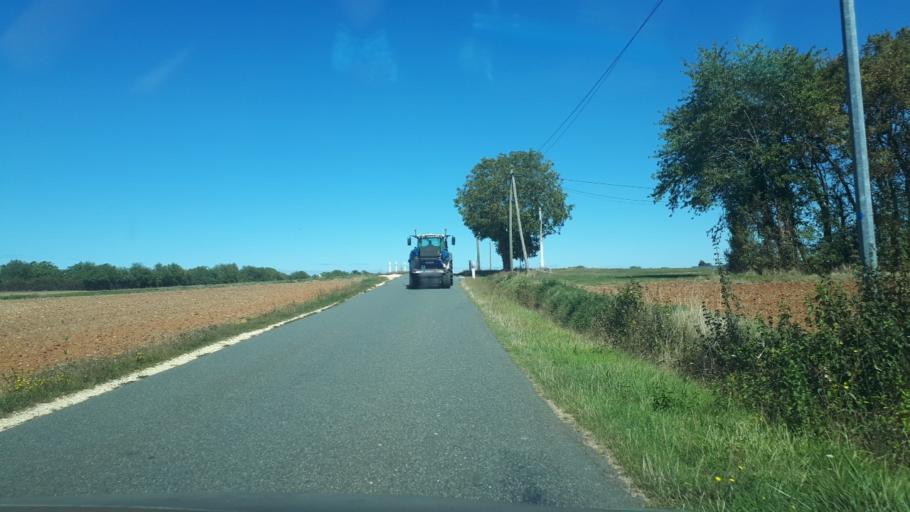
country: FR
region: Centre
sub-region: Departement du Cher
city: Sainte-Solange
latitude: 47.1552
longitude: 2.5643
